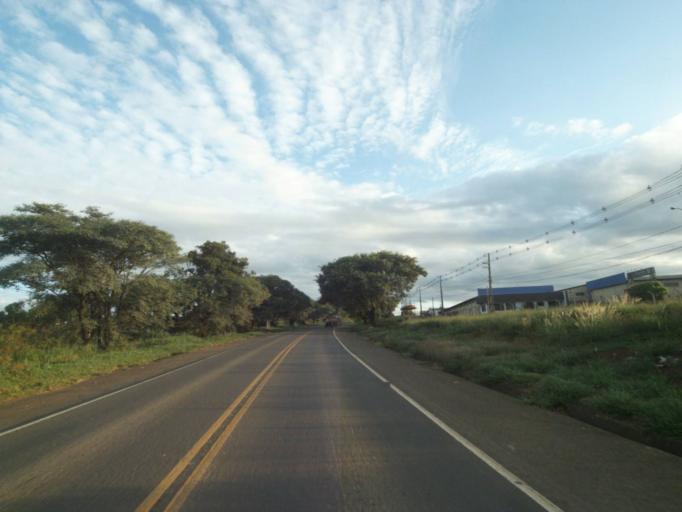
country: BR
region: Parana
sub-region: Telemaco Borba
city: Telemaco Borba
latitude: -24.3562
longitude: -50.6586
